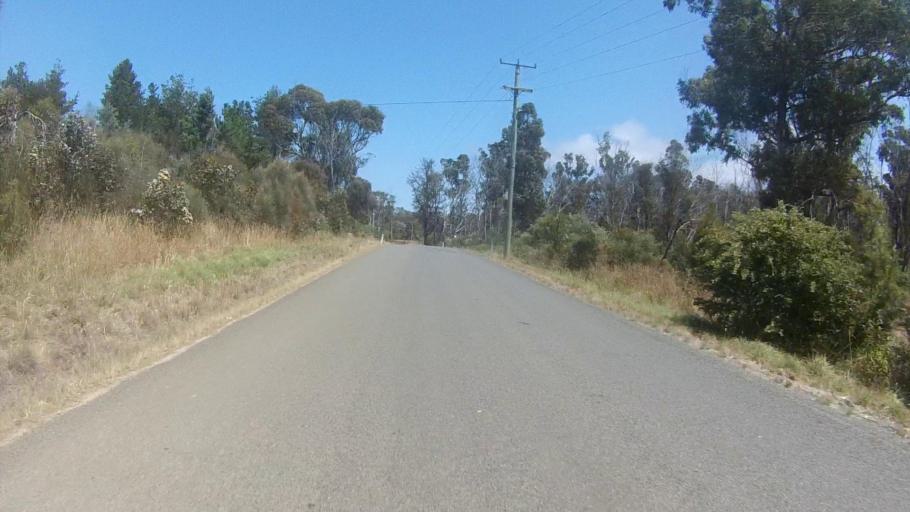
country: AU
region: Tasmania
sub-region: Sorell
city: Sorell
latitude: -42.8553
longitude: 147.8381
